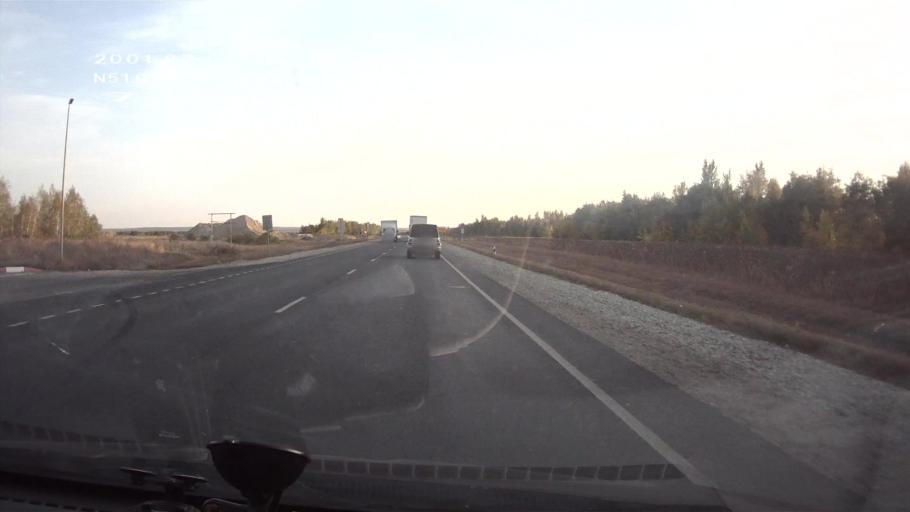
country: RU
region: Saratov
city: Krasnoarmeysk
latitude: 51.0265
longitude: 45.6235
